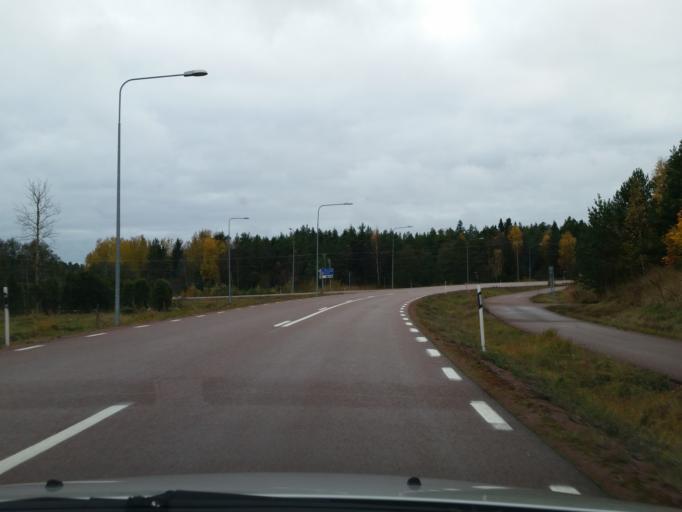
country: AX
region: Alands landsbygd
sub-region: Lumparland
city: Lumparland
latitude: 60.0865
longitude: 20.2583
